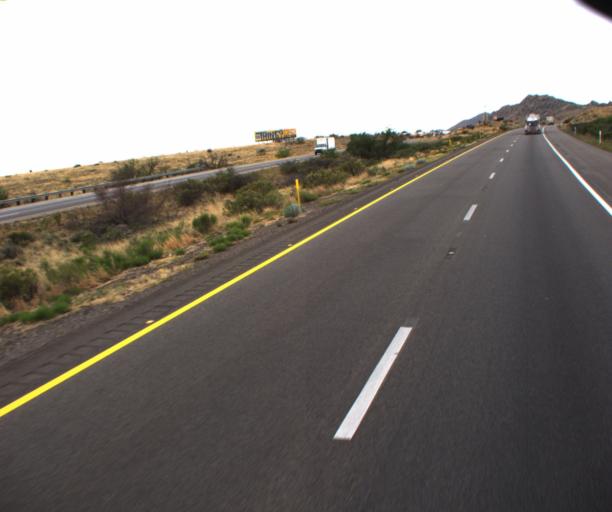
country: US
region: Arizona
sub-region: Cochise County
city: Saint David
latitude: 32.0856
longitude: -110.0448
